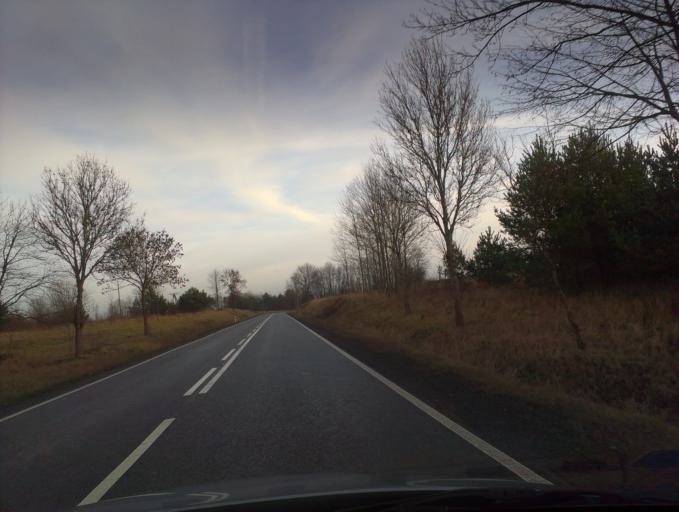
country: PL
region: West Pomeranian Voivodeship
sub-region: Powiat szczecinecki
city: Szczecinek
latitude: 53.7364
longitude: 16.7865
